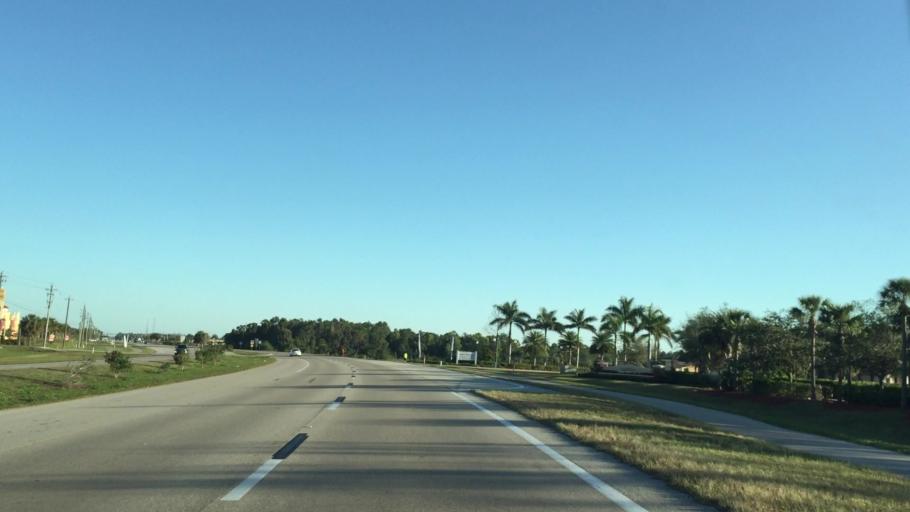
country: US
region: Florida
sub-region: Lee County
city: Fort Myers
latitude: 26.5960
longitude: -81.8116
